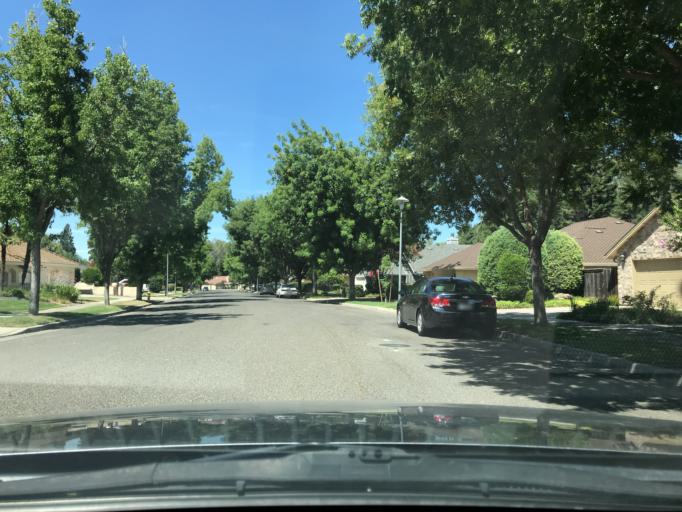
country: US
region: California
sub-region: Merced County
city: Merced
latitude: 37.3263
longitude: -120.4913
